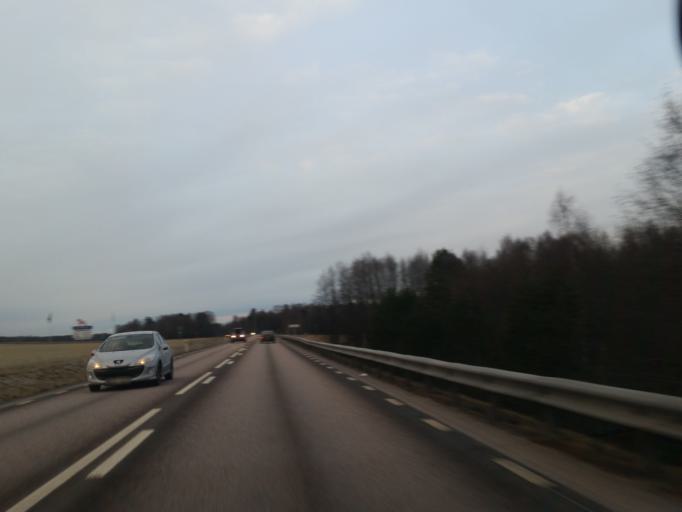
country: SE
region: Dalarna
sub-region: Leksand Municipality
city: Smedby
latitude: 60.7046
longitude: 15.0492
